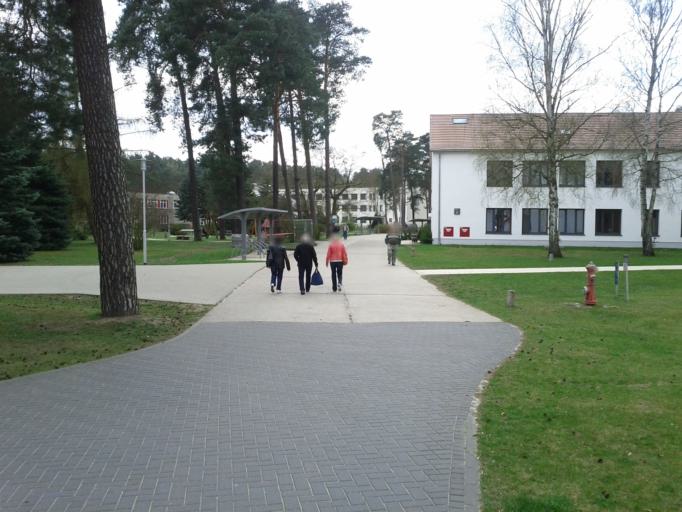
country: DE
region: Brandenburg
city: Bad Saarow
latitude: 52.2844
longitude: 14.0640
